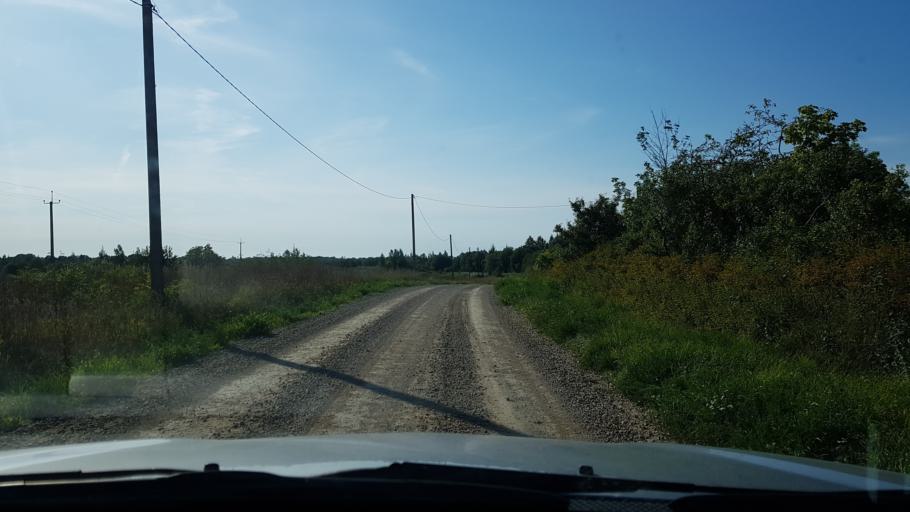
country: EE
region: Ida-Virumaa
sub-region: Narva-Joesuu linn
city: Narva-Joesuu
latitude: 59.4089
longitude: 28.0205
